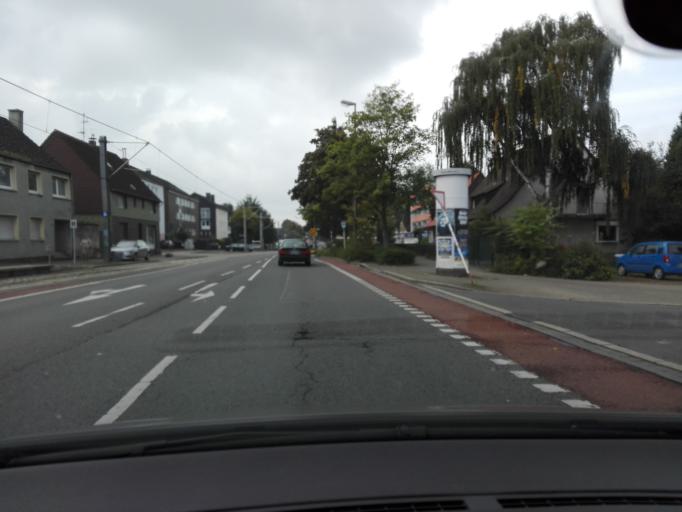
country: DE
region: North Rhine-Westphalia
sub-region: Regierungsbezirk Arnsberg
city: Holzwickede
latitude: 51.5333
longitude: 7.6188
